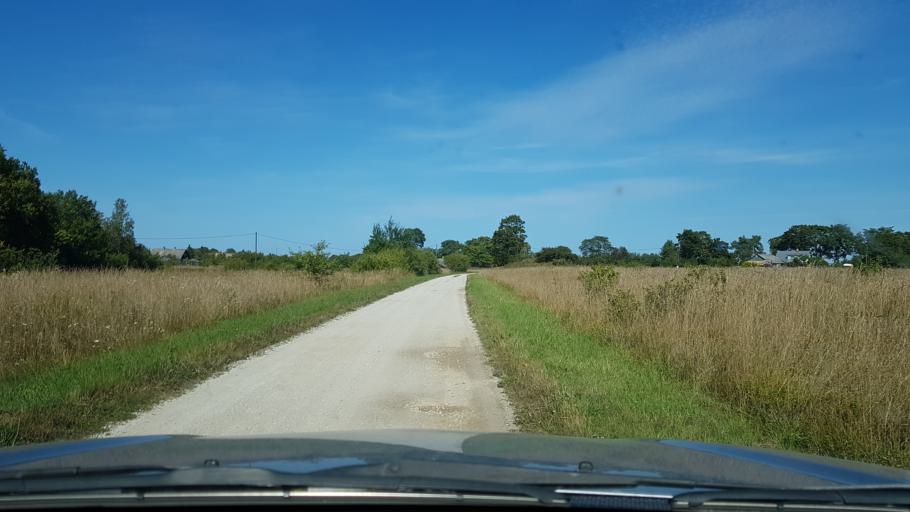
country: EE
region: Ida-Virumaa
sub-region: Sillamaee linn
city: Sillamae
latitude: 59.3814
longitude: 27.8109
